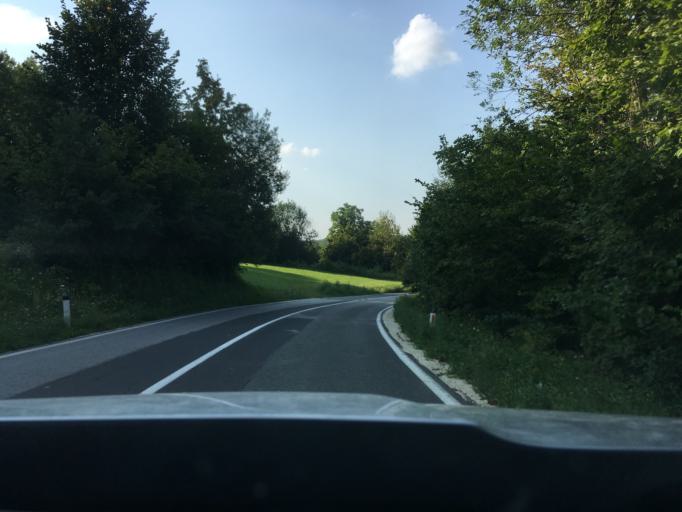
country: SI
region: Novo Mesto
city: Novo Mesto
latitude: 45.7469
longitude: 15.2082
